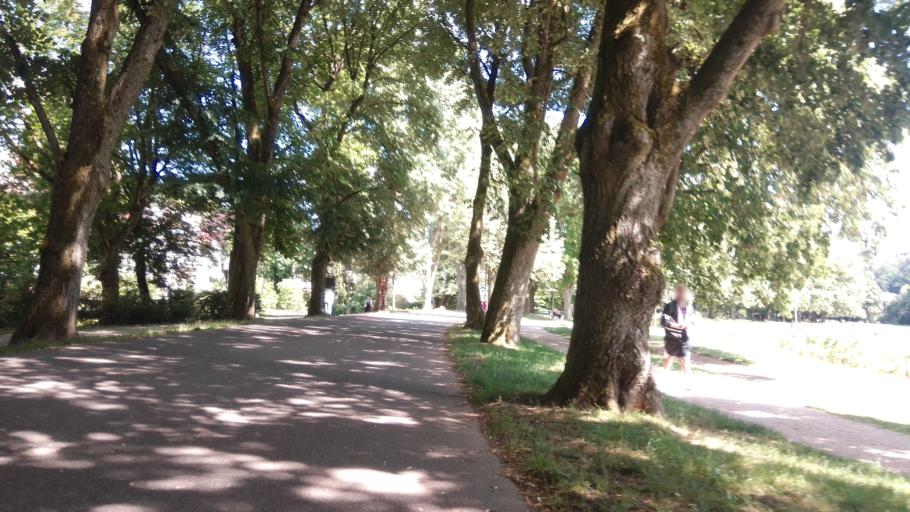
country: DE
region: Baden-Wuerttemberg
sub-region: Karlsruhe Region
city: Baden-Baden
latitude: 48.7501
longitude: 8.2501
